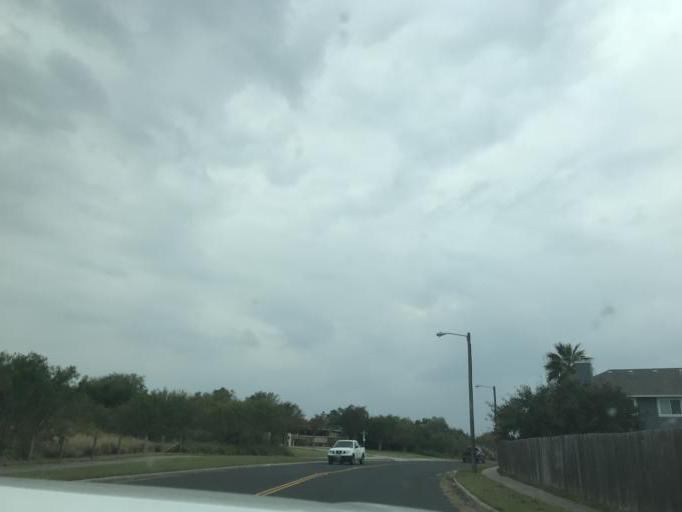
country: US
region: Texas
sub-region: Nueces County
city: Corpus Christi
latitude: 27.6662
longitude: -97.3440
